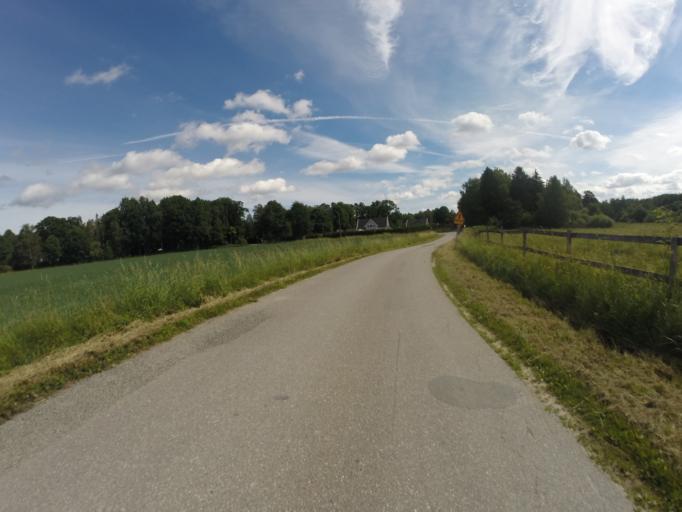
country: SE
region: Soedermanland
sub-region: Eskilstuna Kommun
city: Kvicksund
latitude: 59.4440
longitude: 16.3091
